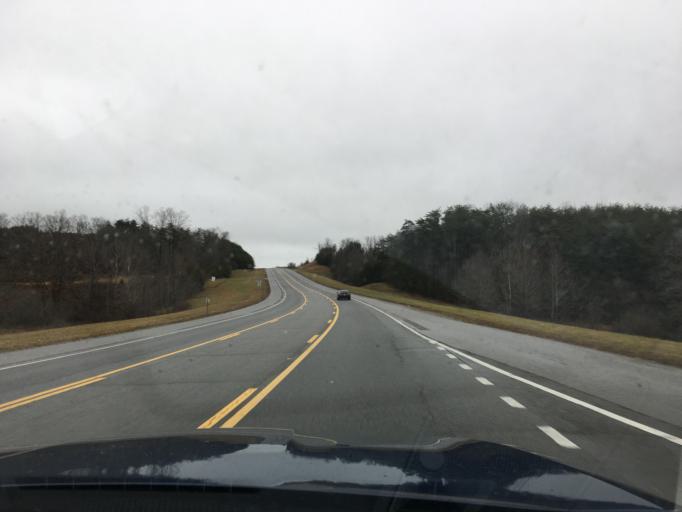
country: US
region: Tennessee
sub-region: Cumberland County
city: Crossville
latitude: 35.9361
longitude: -85.0032
